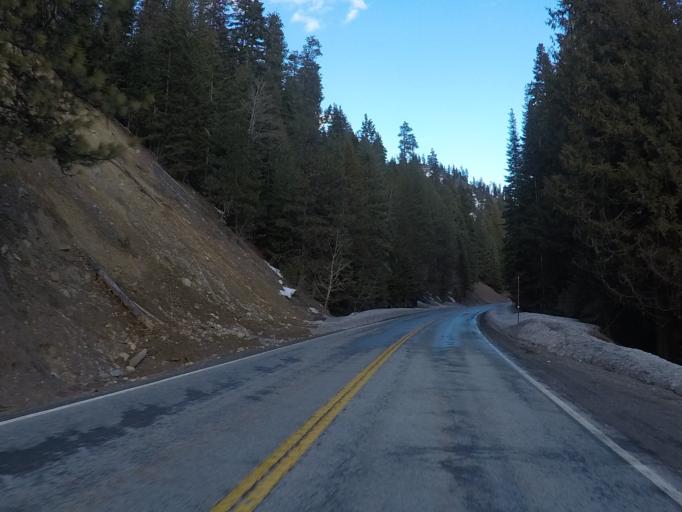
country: US
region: Montana
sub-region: Ravalli County
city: Hamilton
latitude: 46.5176
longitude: -114.7395
